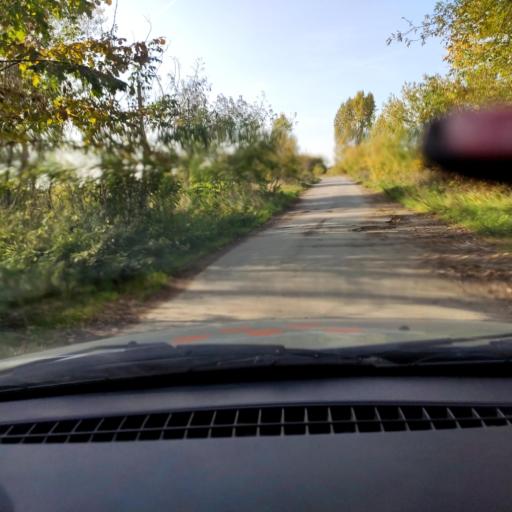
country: RU
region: Bashkortostan
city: Iglino
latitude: 54.7972
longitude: 56.2231
